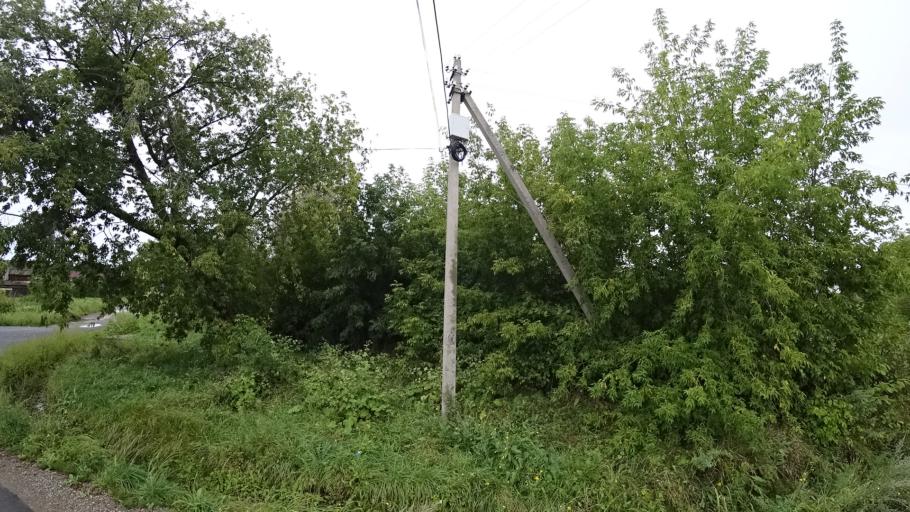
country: RU
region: Primorskiy
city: Monastyrishche
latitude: 44.1969
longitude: 132.4975
